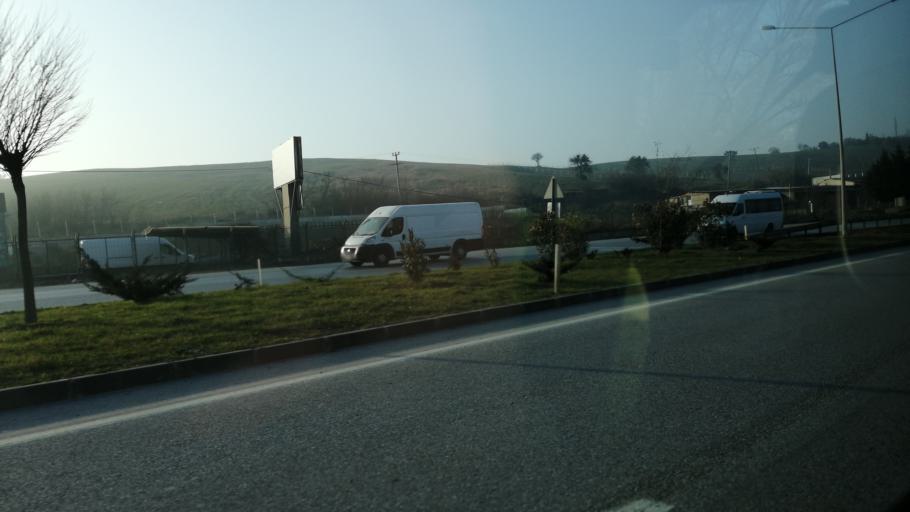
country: TR
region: Yalova
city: Yalova
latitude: 40.6216
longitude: 29.2711
